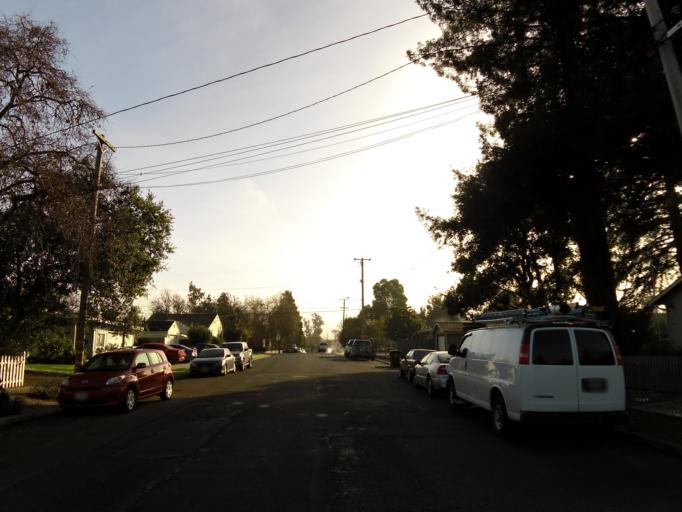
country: US
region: California
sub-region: Napa County
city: Napa
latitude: 38.2880
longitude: -122.2892
